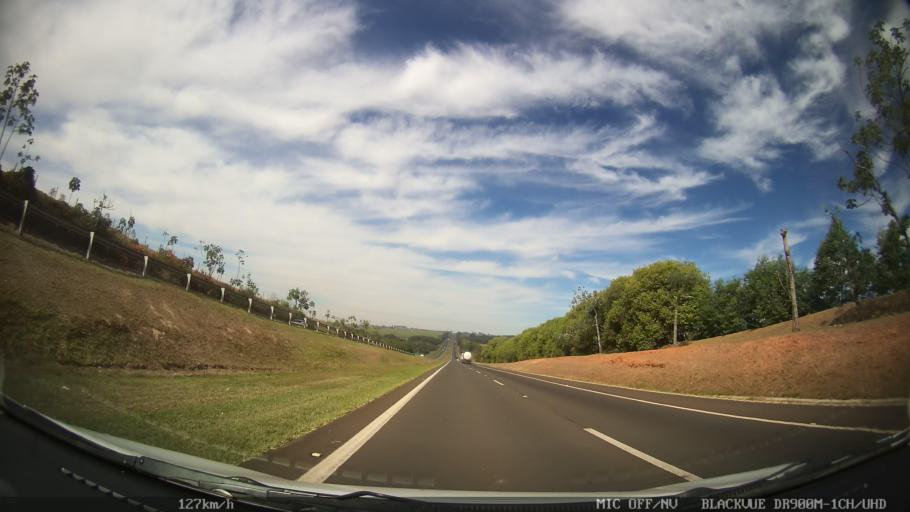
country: BR
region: Sao Paulo
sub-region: Matao
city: Matao
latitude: -21.6106
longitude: -48.4234
